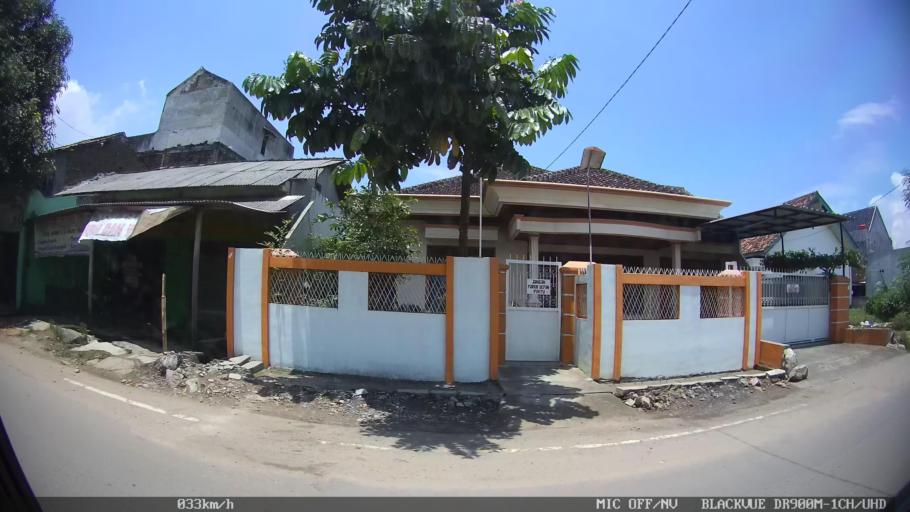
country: ID
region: Lampung
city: Kedaton
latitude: -5.3838
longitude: 105.2881
